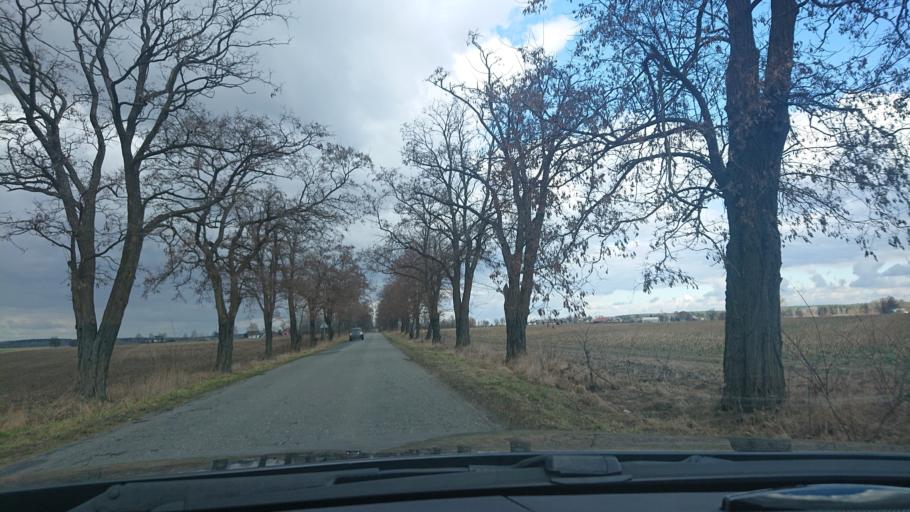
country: PL
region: Greater Poland Voivodeship
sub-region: Powiat gnieznienski
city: Niechanowo
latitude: 52.5755
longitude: 17.7068
